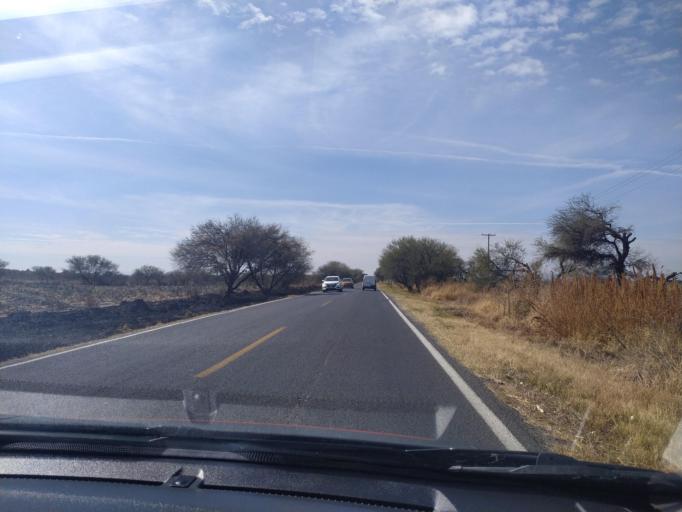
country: MX
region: Guanajuato
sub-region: San Francisco del Rincon
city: San Ignacio de Hidalgo
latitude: 20.9258
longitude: -101.8529
